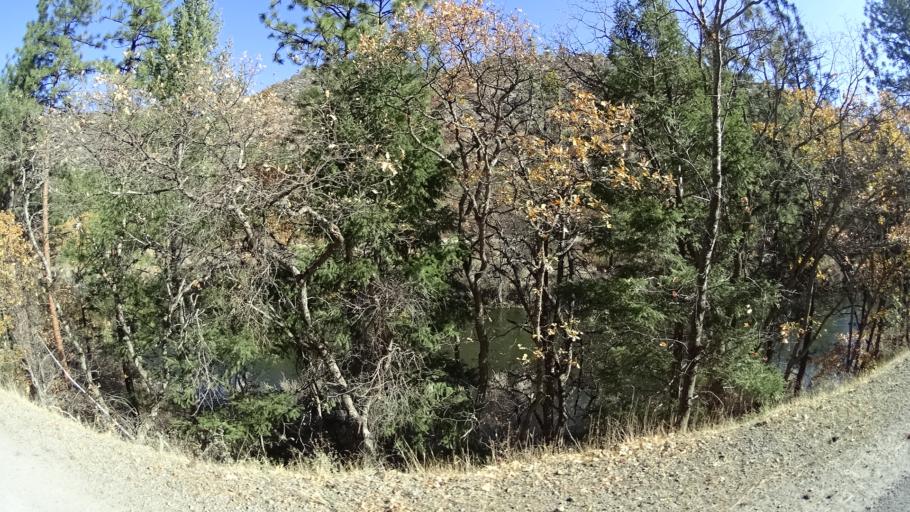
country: US
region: California
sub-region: Siskiyou County
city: Yreka
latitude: 41.8528
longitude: -122.6955
